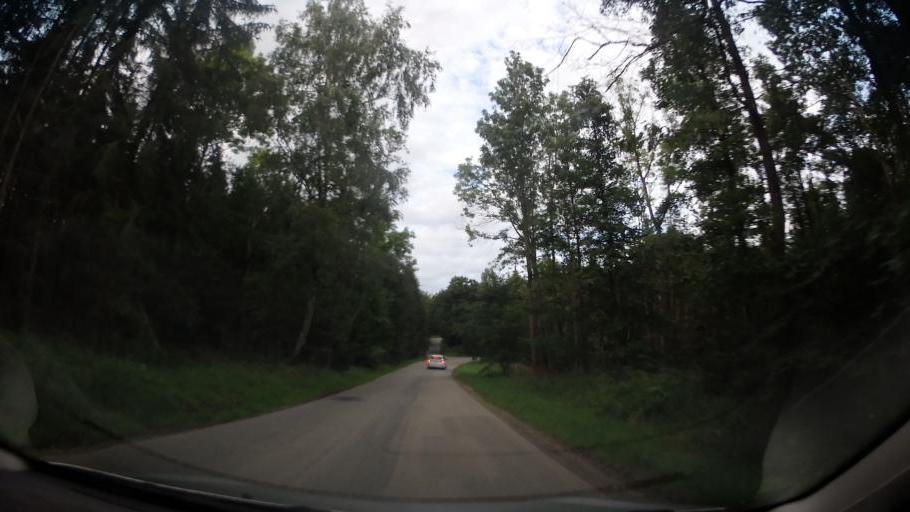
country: CZ
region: Olomoucky
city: Horni Stepanov
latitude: 49.5508
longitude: 16.7354
